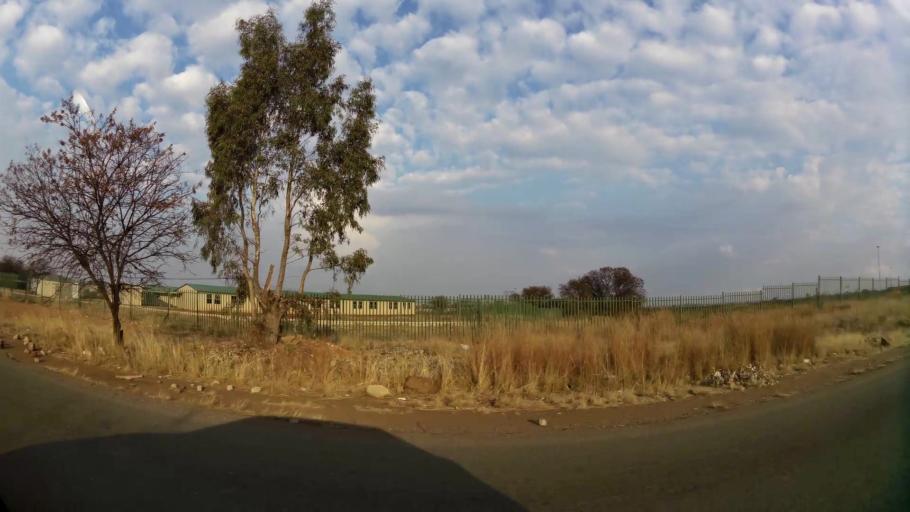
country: ZA
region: Gauteng
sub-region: Sedibeng District Municipality
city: Vereeniging
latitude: -26.6516
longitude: 27.8751
